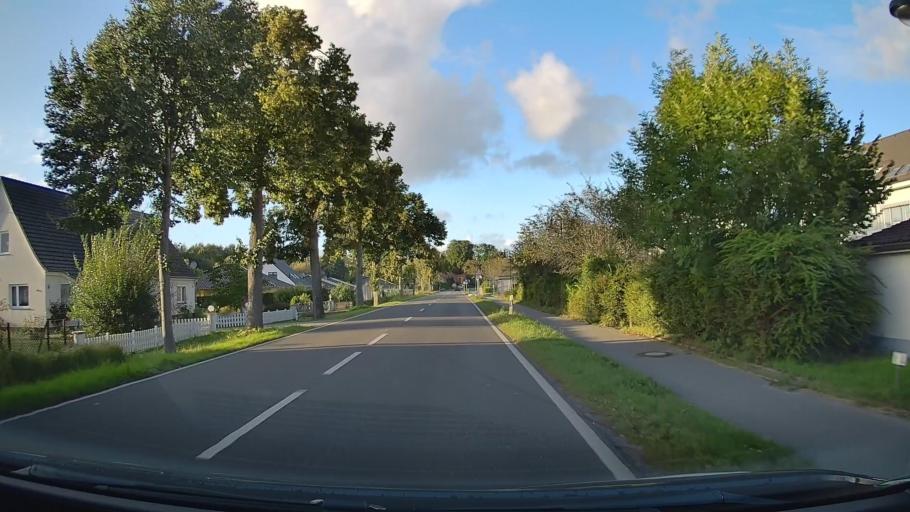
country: DE
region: Mecklenburg-Vorpommern
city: Wendorf
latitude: 54.2589
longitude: 13.0303
